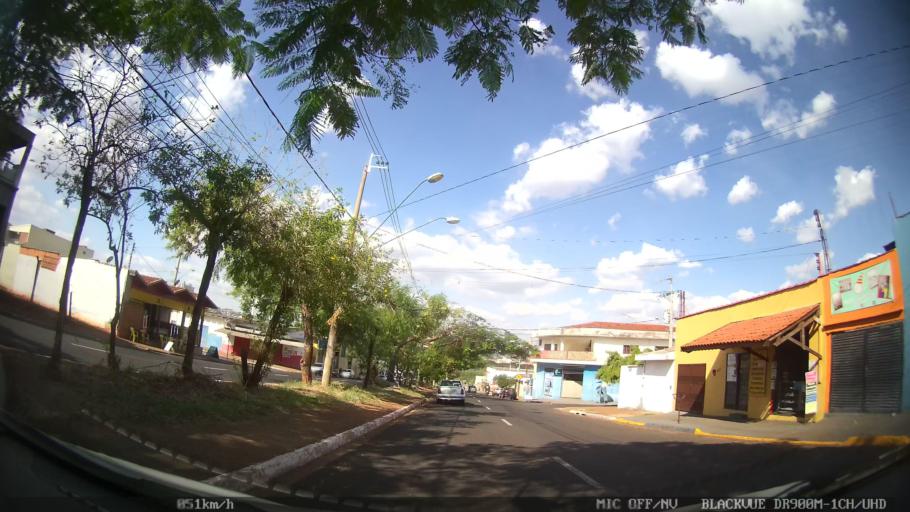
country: BR
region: Sao Paulo
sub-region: Ribeirao Preto
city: Ribeirao Preto
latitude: -21.2014
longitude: -47.8326
